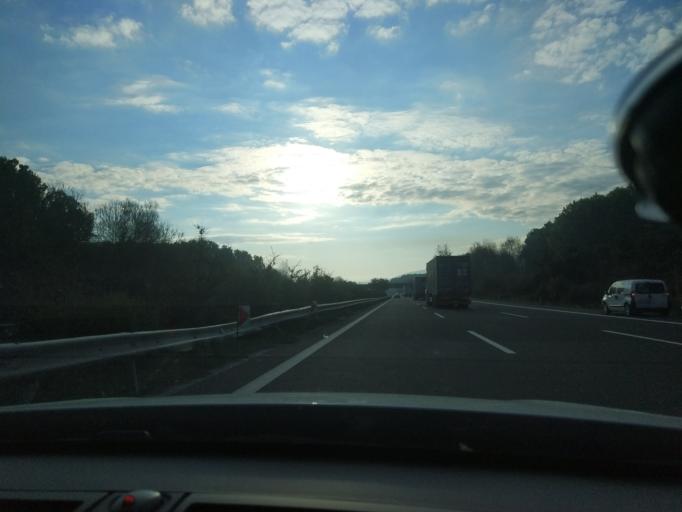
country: TR
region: Duzce
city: Duzce
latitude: 40.8088
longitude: 31.1452
